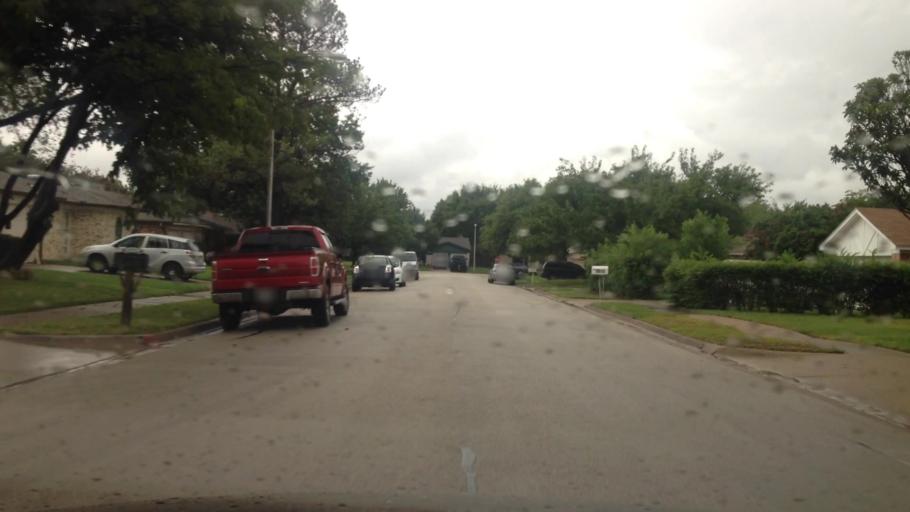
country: US
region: Texas
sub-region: Tarrant County
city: Colleyville
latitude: 32.8685
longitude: -97.1962
